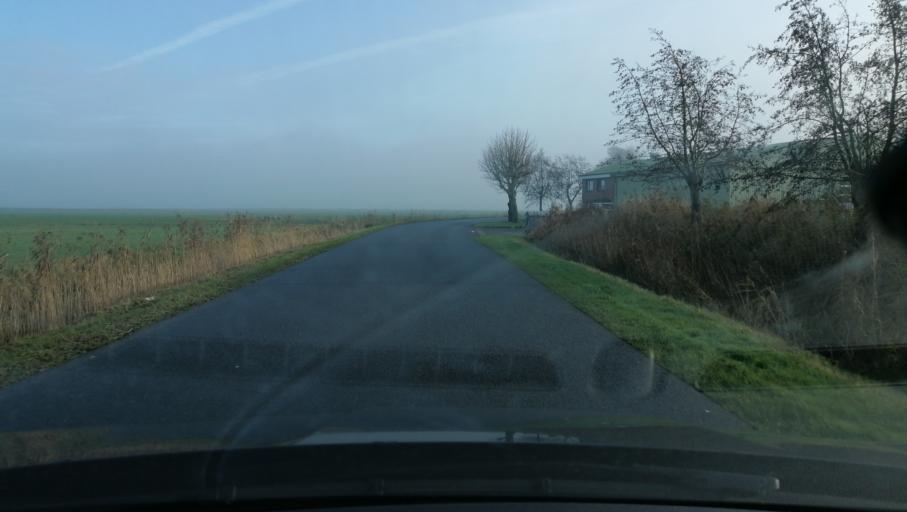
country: DE
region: Schleswig-Holstein
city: Epenwohrden
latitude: 54.1050
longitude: 9.0433
